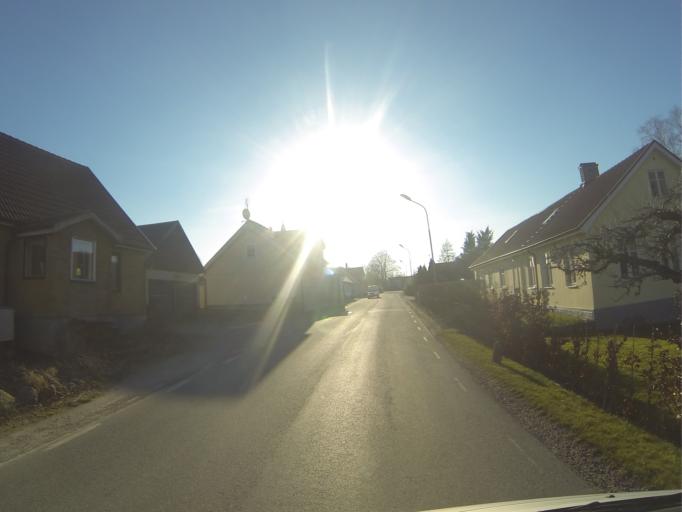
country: SE
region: Skane
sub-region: Horby Kommun
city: Hoerby
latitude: 55.8370
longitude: 13.6235
